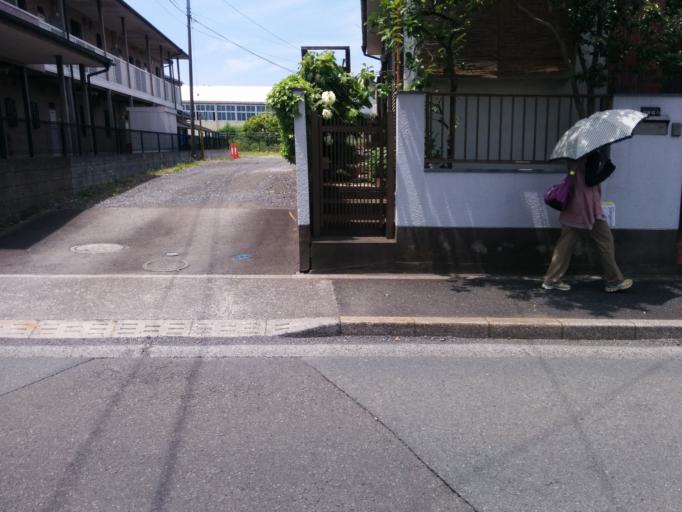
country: JP
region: Tokyo
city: Higashimurayama-shi
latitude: 35.7570
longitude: 139.4797
